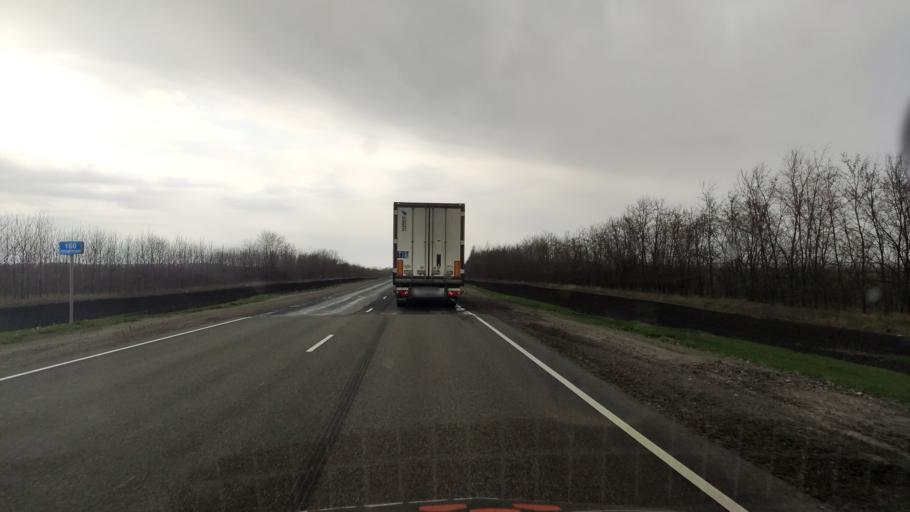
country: RU
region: Voronezj
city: Nizhnedevitsk
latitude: 51.5692
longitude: 38.3374
